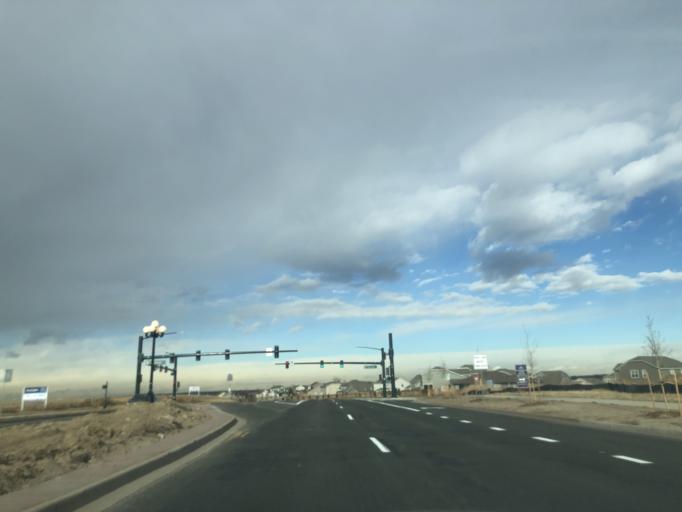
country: US
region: Colorado
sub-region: Douglas County
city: Stonegate
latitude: 39.5554
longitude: -104.8073
